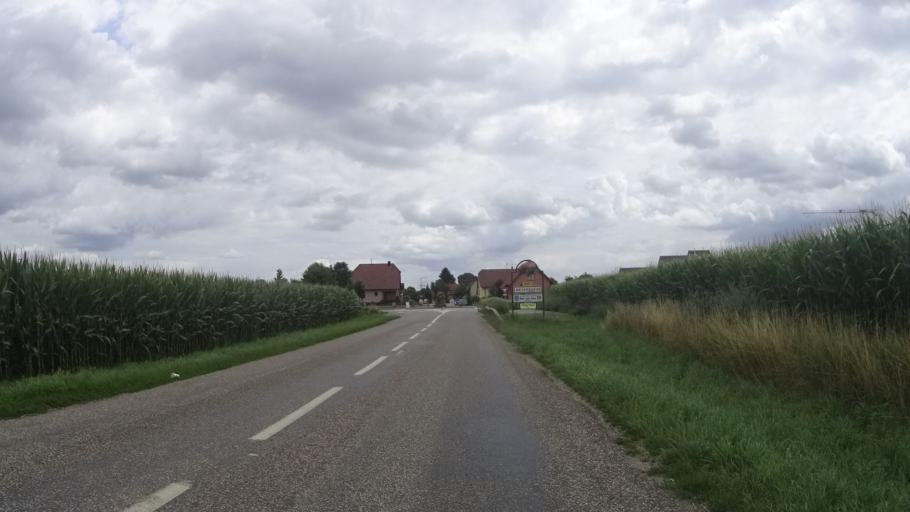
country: FR
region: Alsace
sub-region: Departement du Bas-Rhin
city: Weyersheim
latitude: 48.7172
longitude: 7.7917
